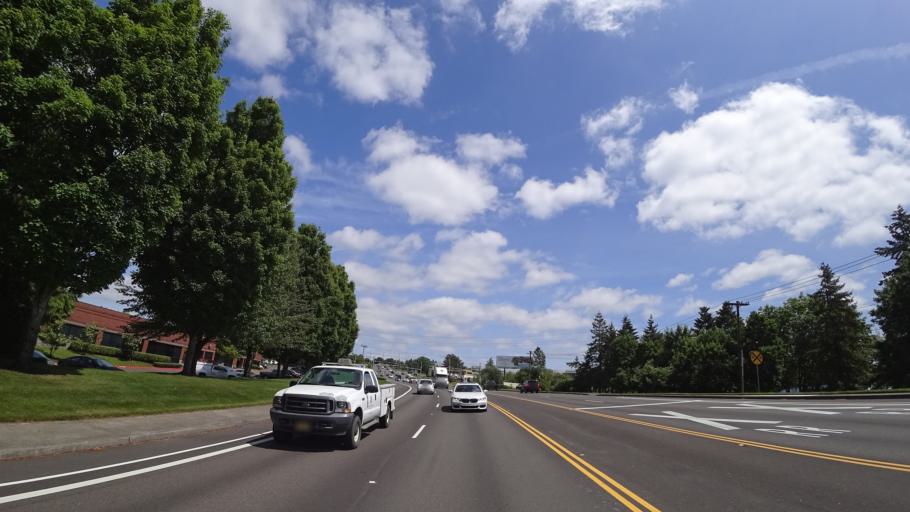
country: US
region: Oregon
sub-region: Washington County
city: Tigard
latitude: 45.4482
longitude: -122.7879
